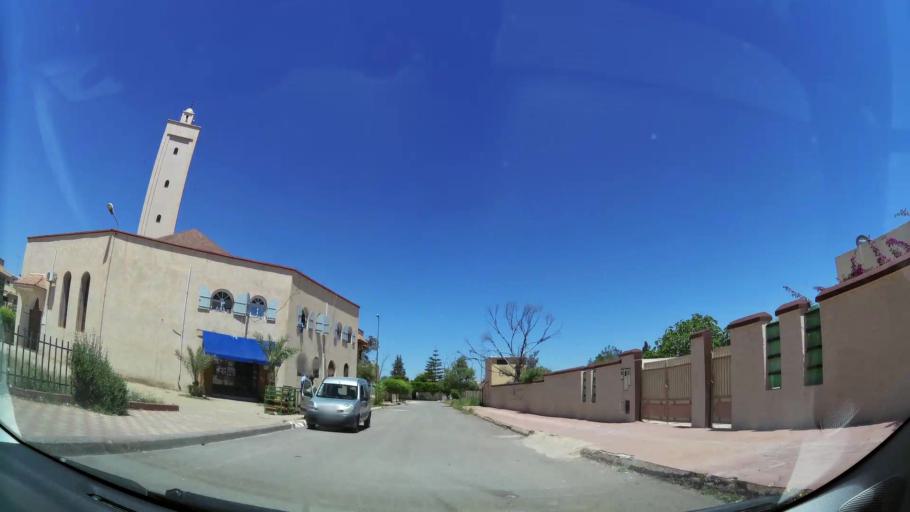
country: MA
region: Oriental
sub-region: Oujda-Angad
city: Oujda
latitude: 34.6696
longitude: -1.8707
